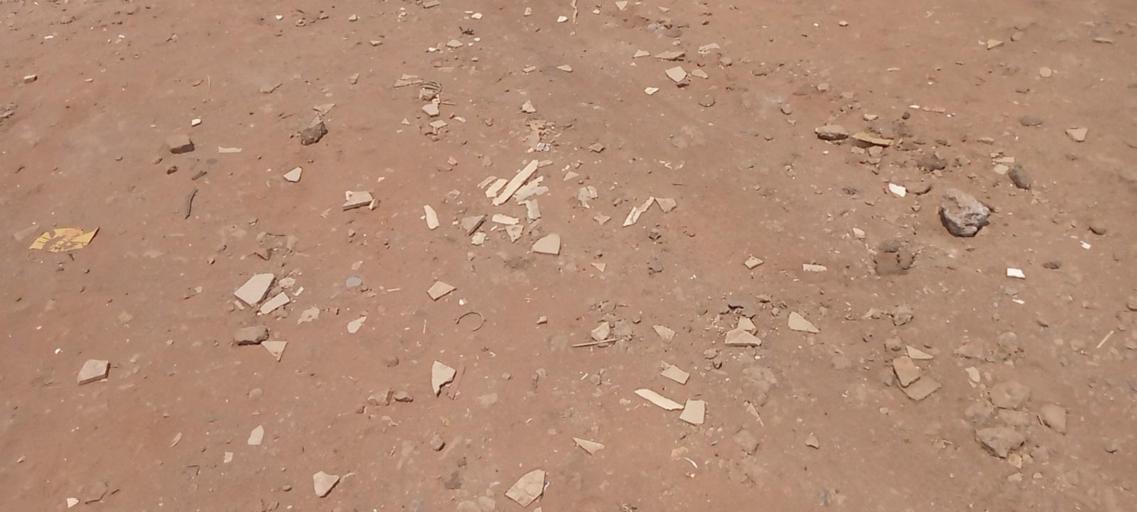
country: ZM
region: Lusaka
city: Lusaka
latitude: -15.3999
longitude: 28.3460
